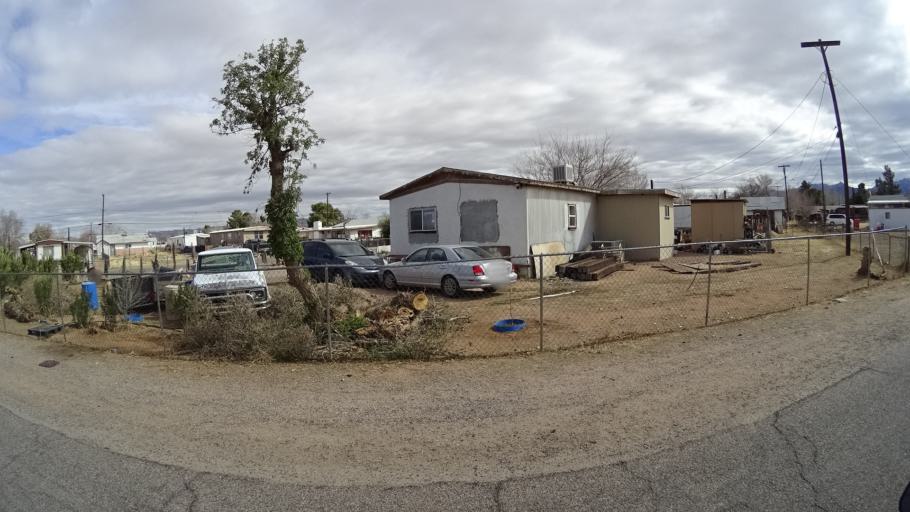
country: US
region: Arizona
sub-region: Mohave County
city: New Kingman-Butler
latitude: 35.2460
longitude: -113.9933
